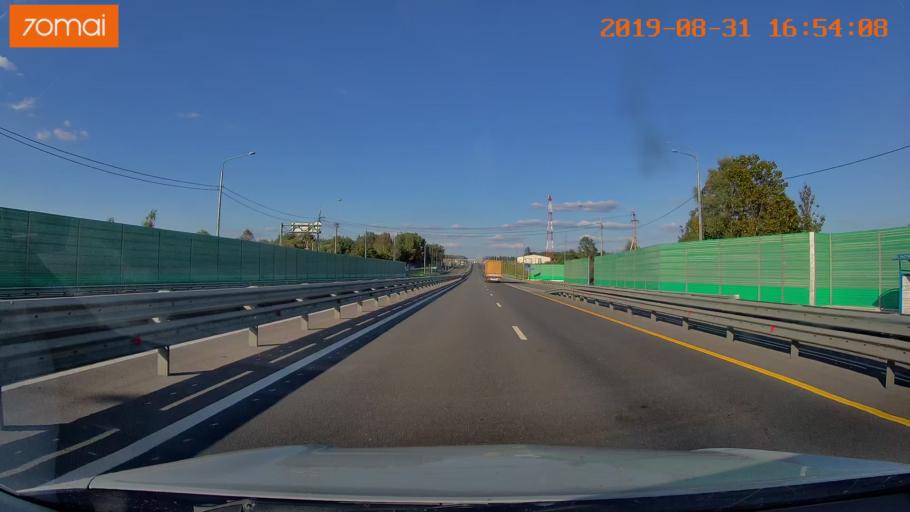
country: RU
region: Kaluga
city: Detchino
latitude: 54.7658
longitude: 36.2264
